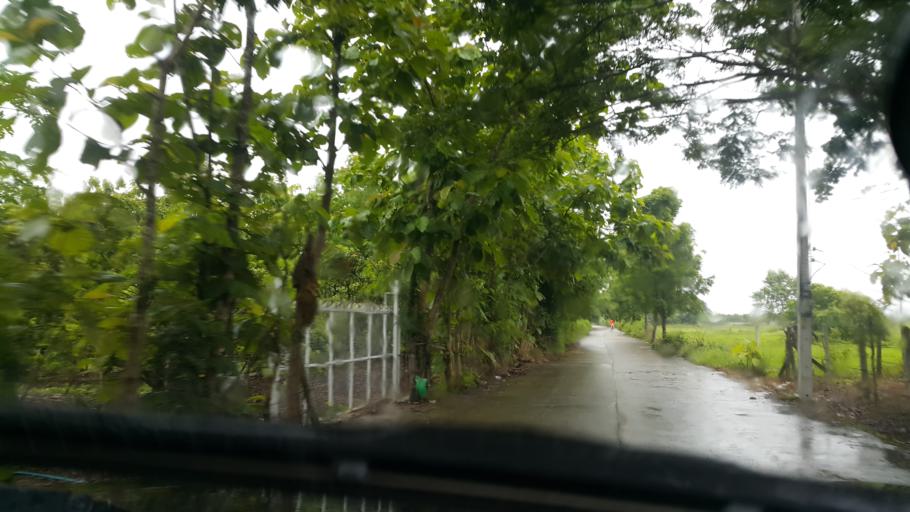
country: TH
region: Lamphun
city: Ban Thi
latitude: 18.6279
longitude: 99.1157
